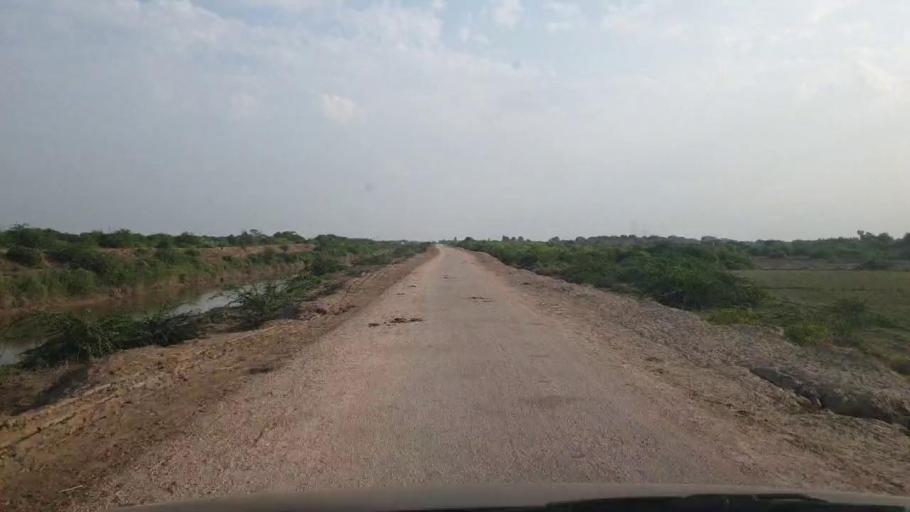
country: PK
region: Sindh
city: Badin
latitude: 24.5368
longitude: 68.6760
